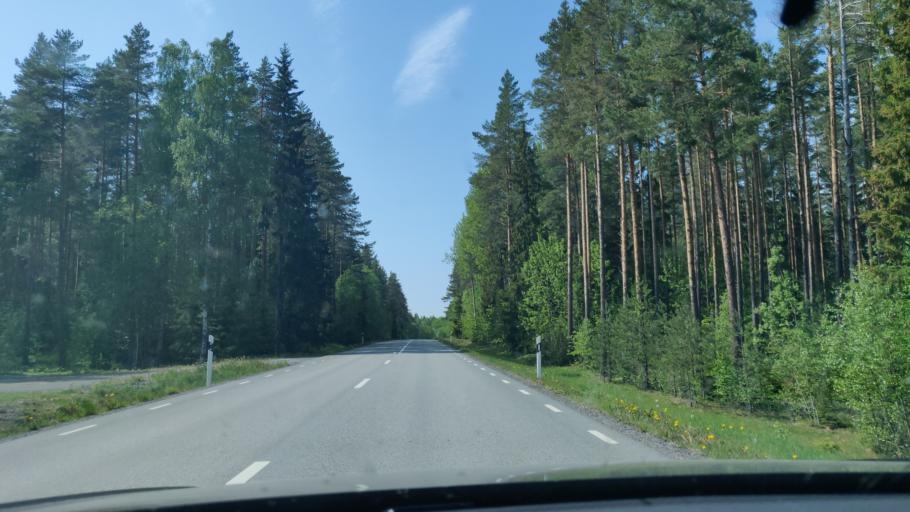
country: SE
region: Uppsala
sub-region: Heby Kommun
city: OEstervala
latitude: 60.1432
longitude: 17.2091
